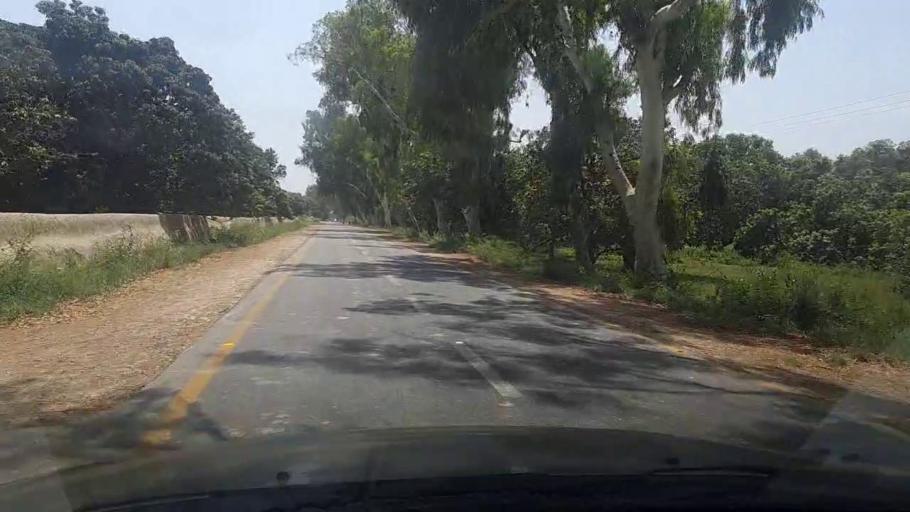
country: PK
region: Sindh
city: Tando Jam
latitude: 25.3492
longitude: 68.5112
